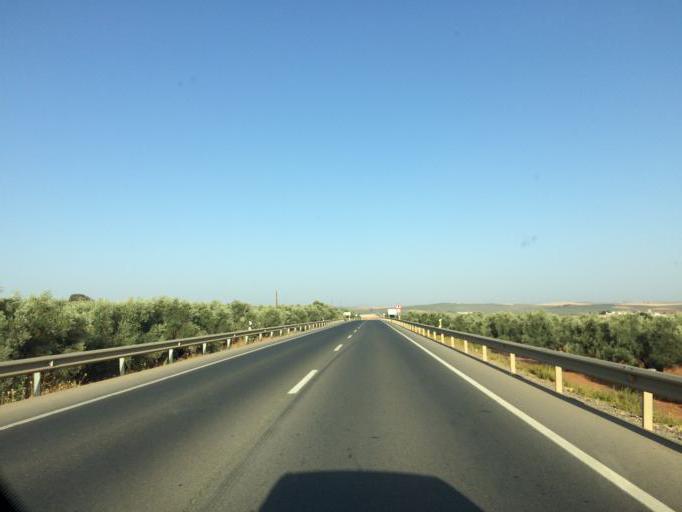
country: ES
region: Andalusia
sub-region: Provincia de Malaga
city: Humilladero
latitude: 37.0553
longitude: -4.7415
